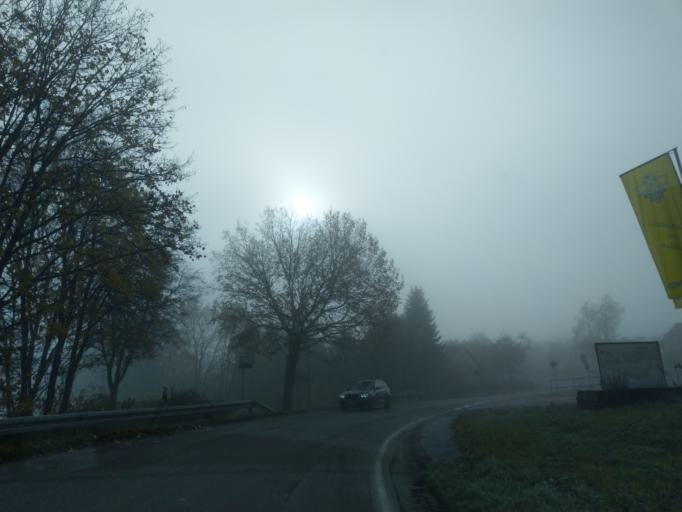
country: DE
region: Bavaria
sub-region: Lower Bavaria
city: Schollnach
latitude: 48.7486
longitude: 13.1859
